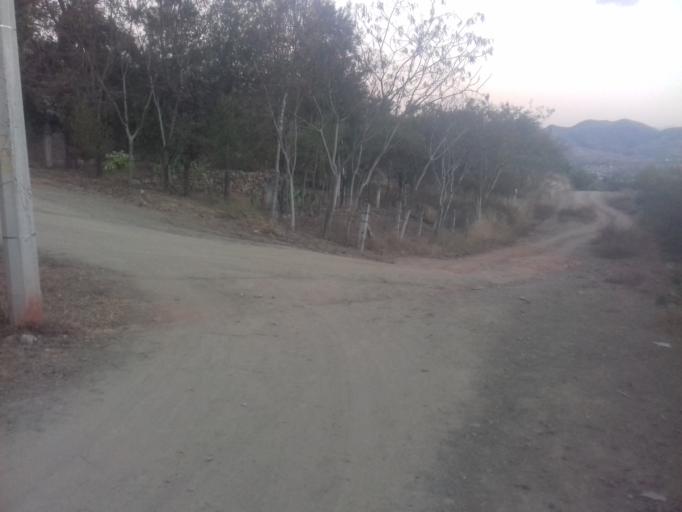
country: MX
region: Oaxaca
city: Ciudad de Huajuapam de Leon
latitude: 17.8232
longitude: -97.7916
